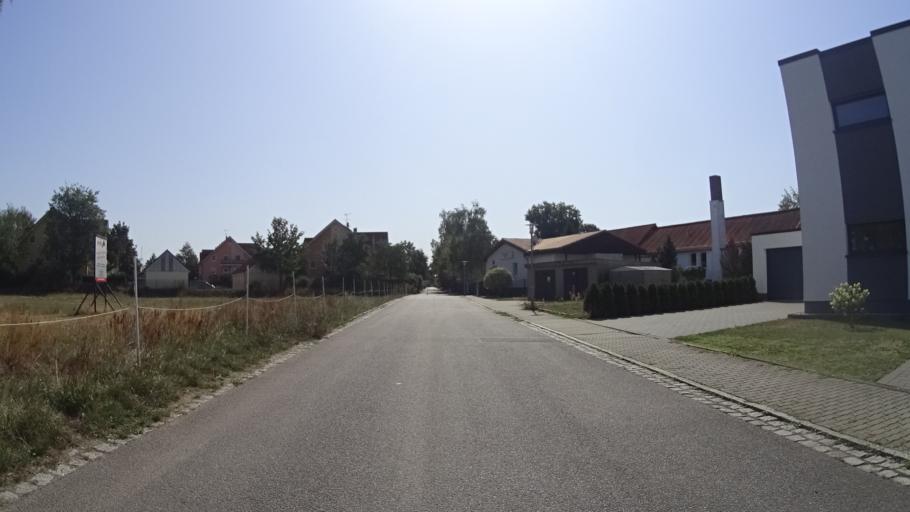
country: DE
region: Brandenburg
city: Werben
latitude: 51.8145
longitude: 14.1917
